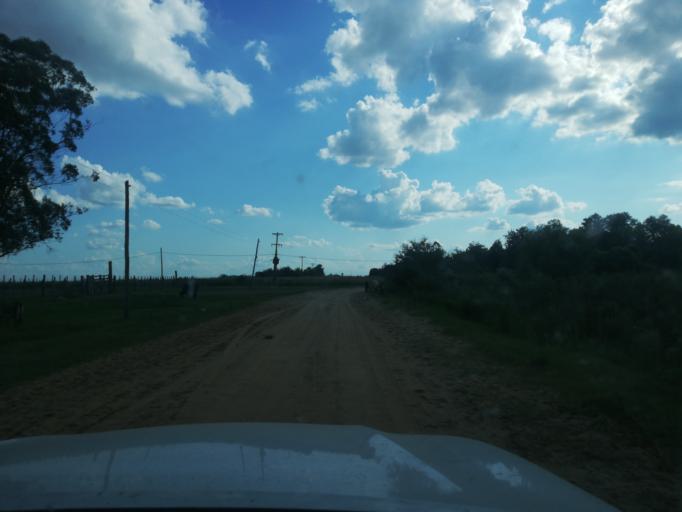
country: AR
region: Corrientes
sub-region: Departamento de San Miguel
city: San Miguel
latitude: -27.9972
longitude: -57.5799
